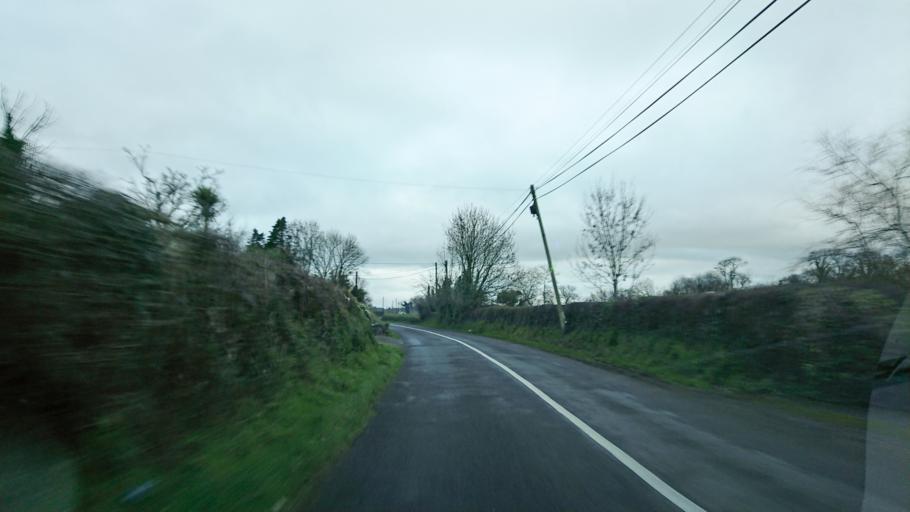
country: IE
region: Munster
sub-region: Waterford
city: Portlaw
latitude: 52.1861
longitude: -7.4086
